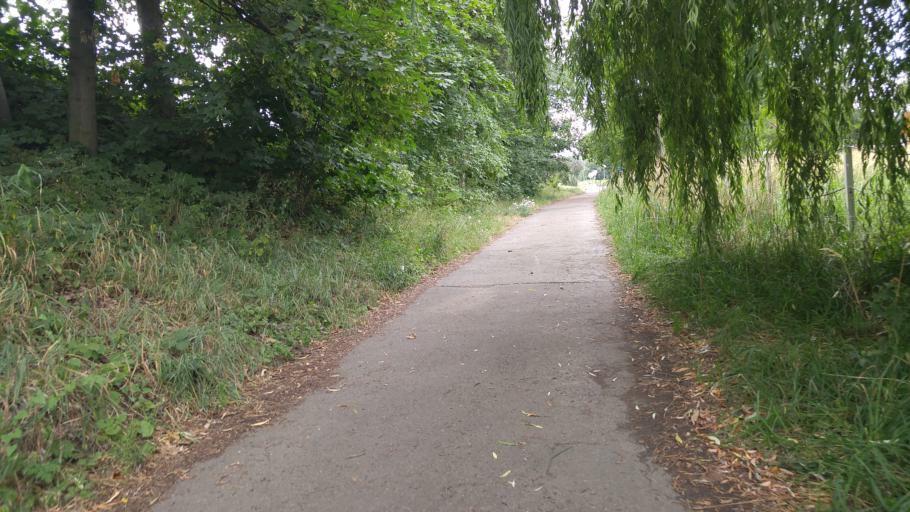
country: CZ
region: Praha
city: Prague
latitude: 50.1114
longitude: 14.4177
